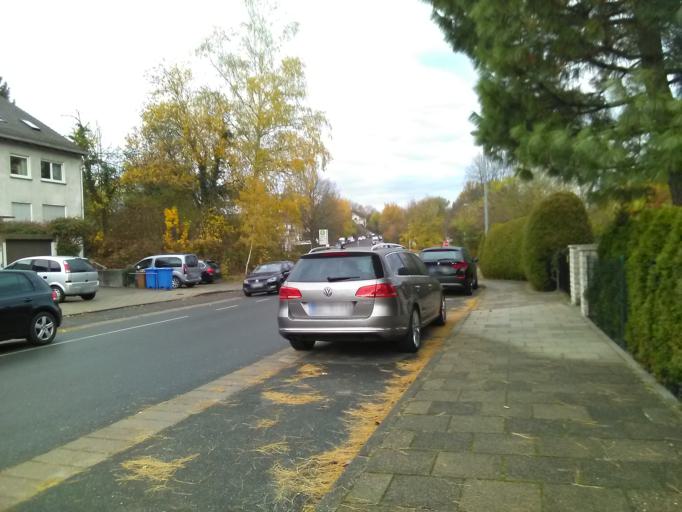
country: DE
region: Bavaria
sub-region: Upper Franconia
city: Bamberg
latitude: 49.8831
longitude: 10.8809
